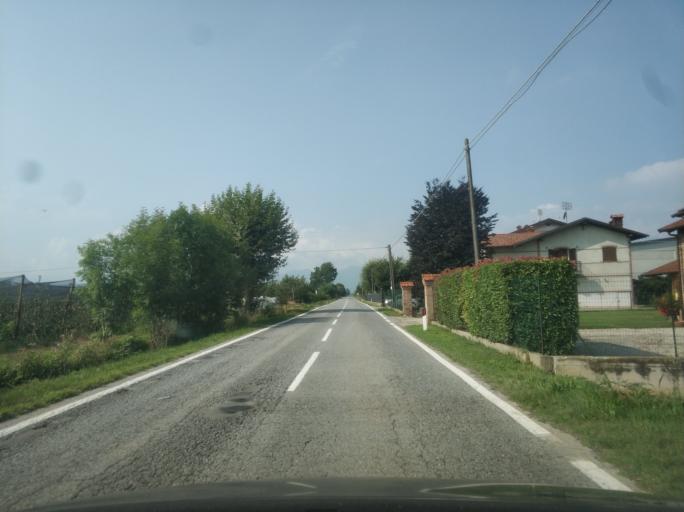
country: IT
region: Piedmont
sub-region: Provincia di Cuneo
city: Roata Rossi
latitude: 44.4689
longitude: 7.5074
